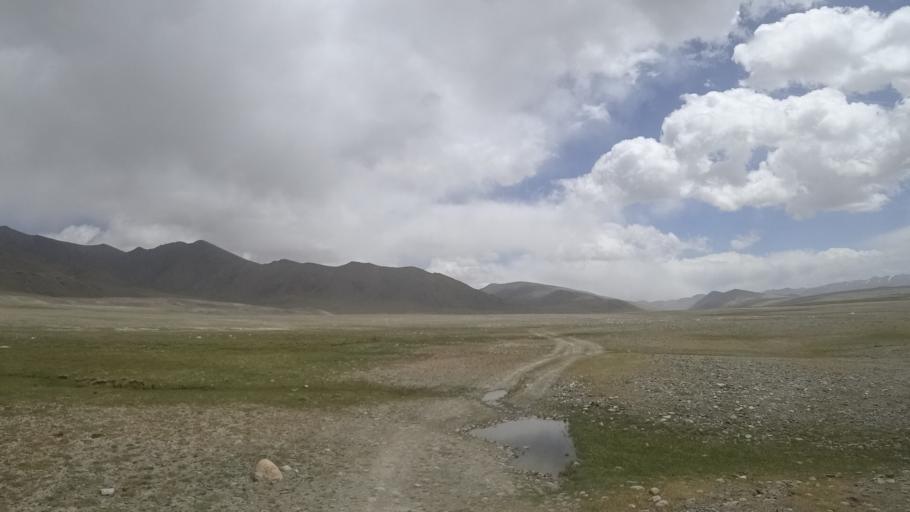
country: TJ
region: Gorno-Badakhshan
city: Murghob
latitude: 37.4887
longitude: 73.9978
